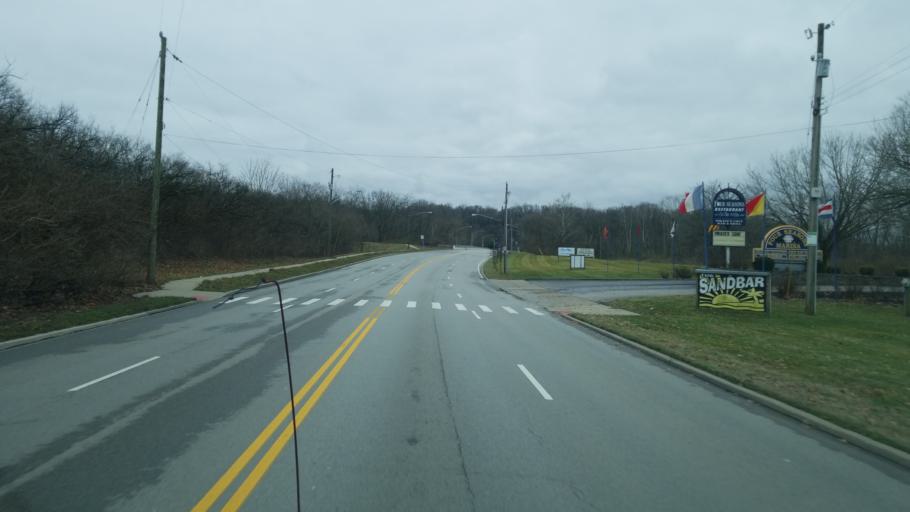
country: US
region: Kentucky
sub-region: Campbell County
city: Fort Thomas
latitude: 39.0880
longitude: -84.4233
